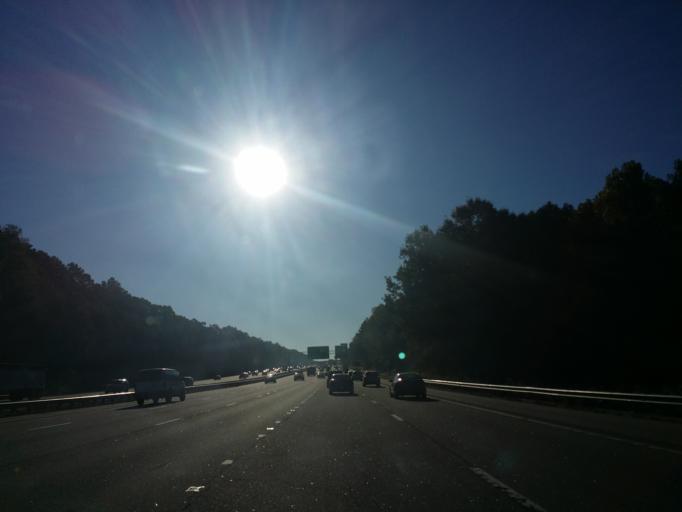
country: US
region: North Carolina
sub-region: Wake County
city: Cary
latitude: 35.8264
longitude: -78.7545
